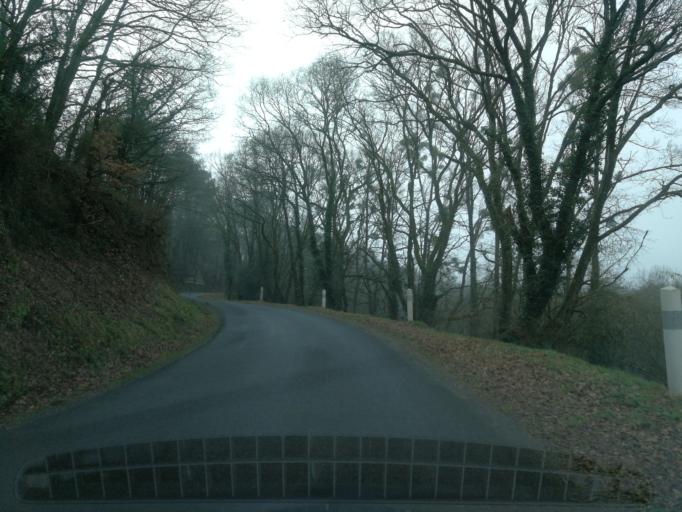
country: FR
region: Brittany
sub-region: Departement du Morbihan
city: La Vraie-Croix
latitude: 47.7318
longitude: -2.5055
